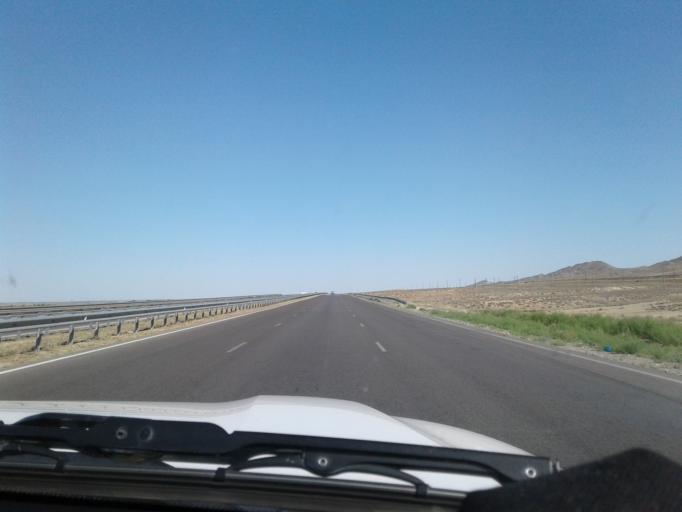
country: IR
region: Razavi Khorasan
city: Dargaz
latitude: 37.6282
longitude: 59.1613
